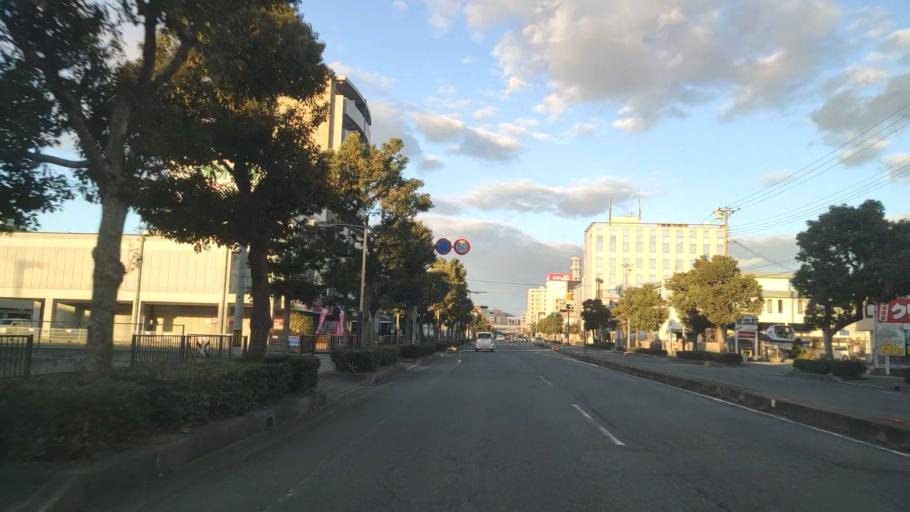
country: JP
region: Hyogo
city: Himeji
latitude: 34.8181
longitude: 134.6911
